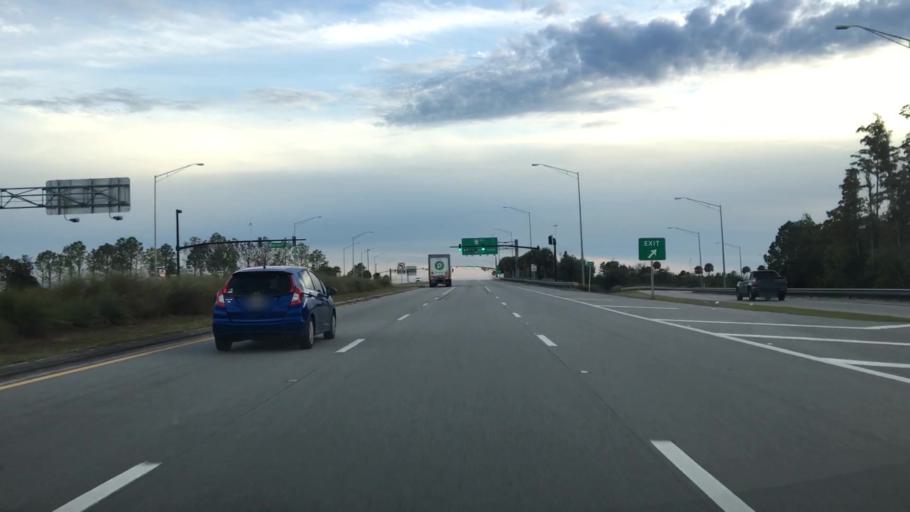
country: US
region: Florida
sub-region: Orange County
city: Conway
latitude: 28.4522
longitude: -81.2862
